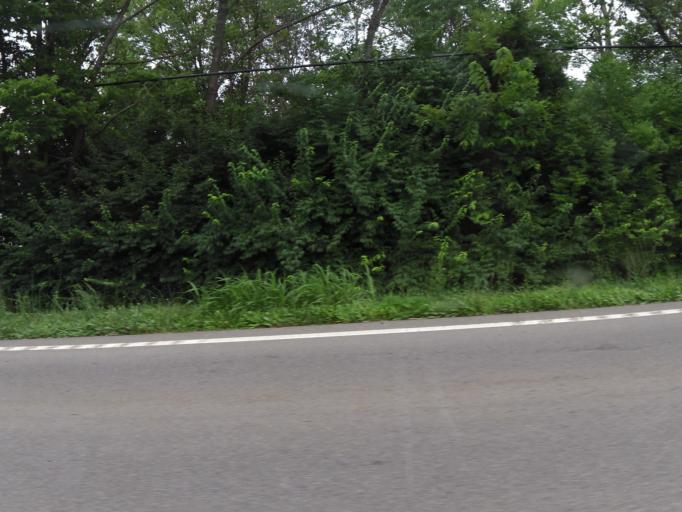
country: US
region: Ohio
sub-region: Warren County
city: Waynesville
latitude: 39.5181
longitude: -84.0507
